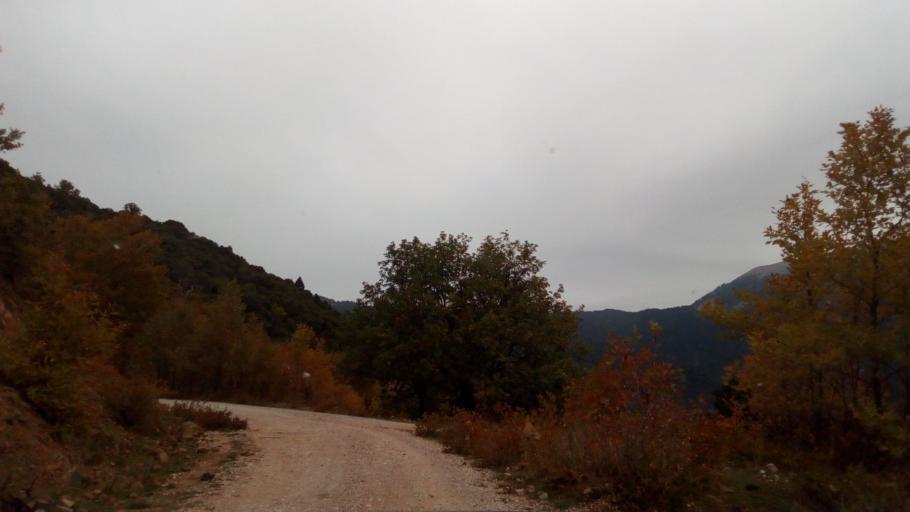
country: GR
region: West Greece
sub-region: Nomos Aitolias kai Akarnanias
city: Thermo
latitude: 38.6003
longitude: 21.8272
